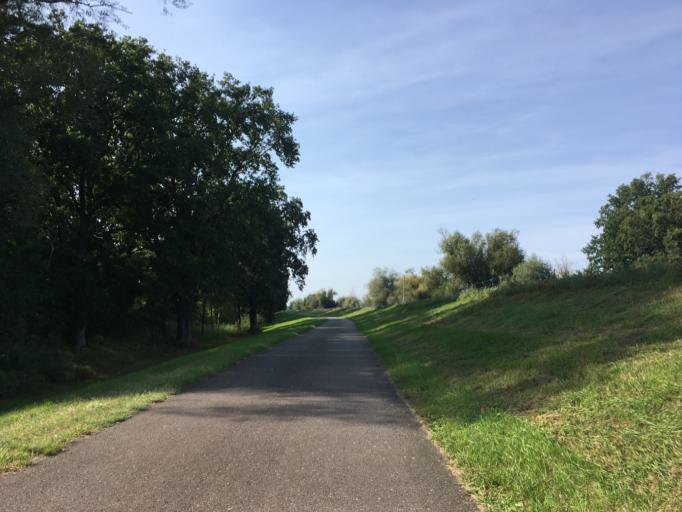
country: DE
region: Brandenburg
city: Vogelsang
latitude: 52.2538
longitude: 14.6816
